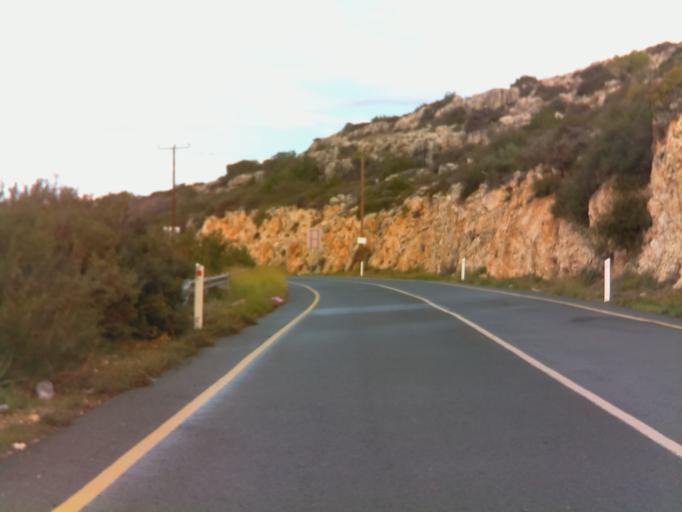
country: CY
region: Pafos
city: Pegeia
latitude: 34.8893
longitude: 32.3700
